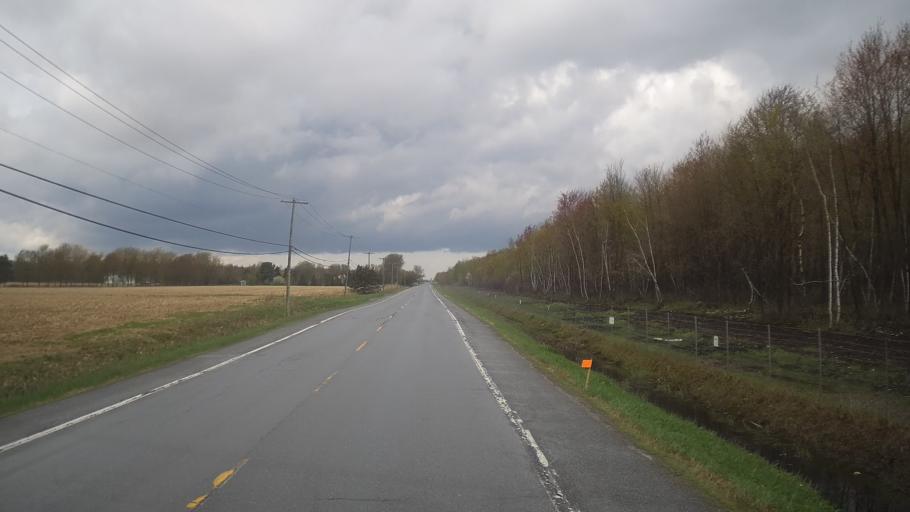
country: CA
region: Quebec
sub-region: Monteregie
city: Farnham
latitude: 45.2967
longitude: -73.0268
